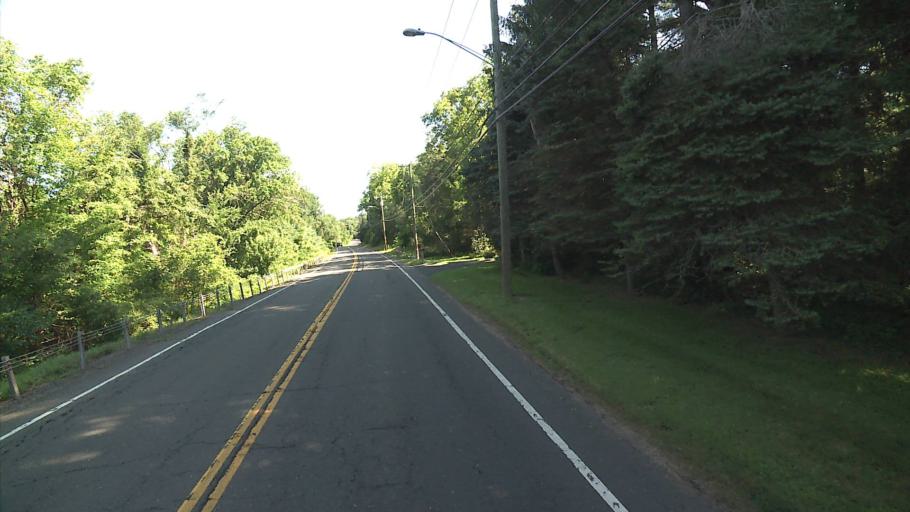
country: US
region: Connecticut
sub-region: Hartford County
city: Farmington
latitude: 41.7493
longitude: -72.8194
